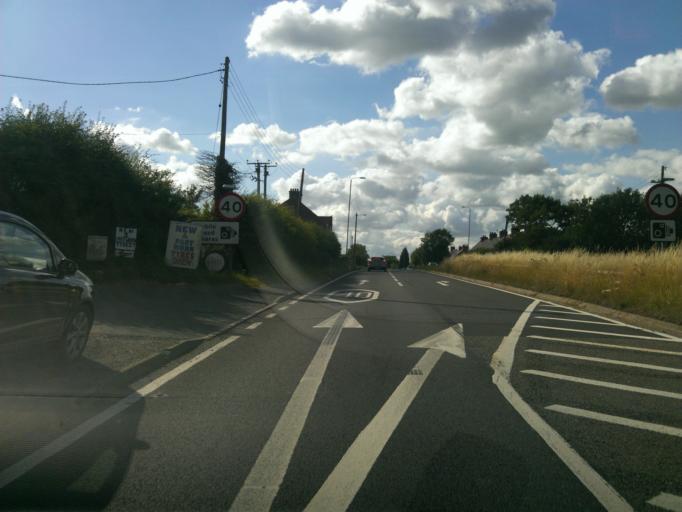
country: GB
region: England
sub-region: Warwickshire
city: Atherstone
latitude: 52.5869
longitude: -1.5789
